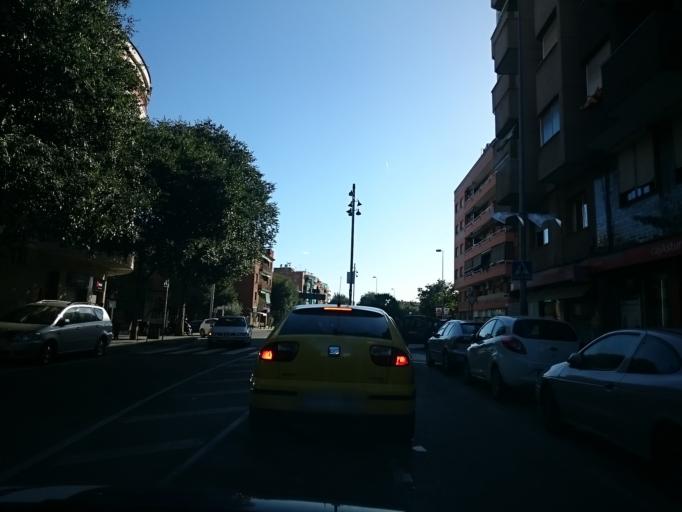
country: ES
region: Catalonia
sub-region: Provincia de Barcelona
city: Gava
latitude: 41.3023
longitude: 2.0072
